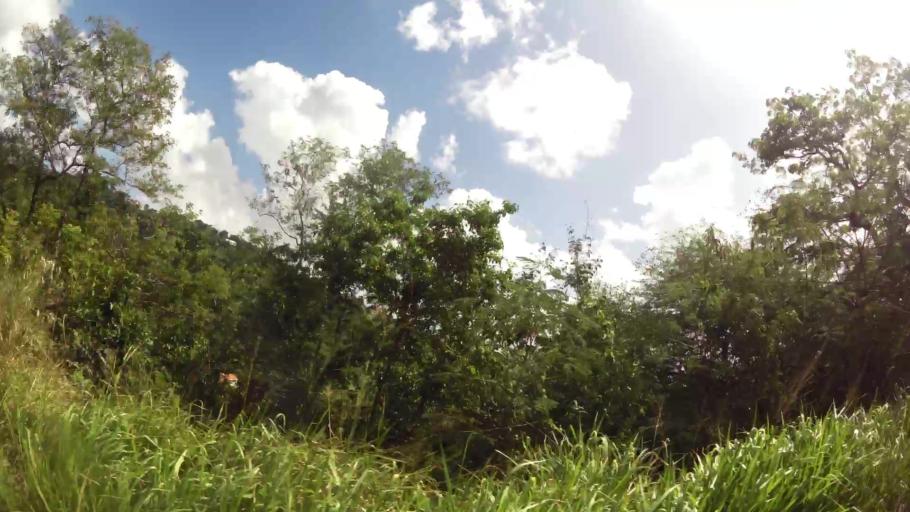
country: MQ
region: Martinique
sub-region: Martinique
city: Fort-de-France
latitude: 14.6377
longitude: -61.1323
